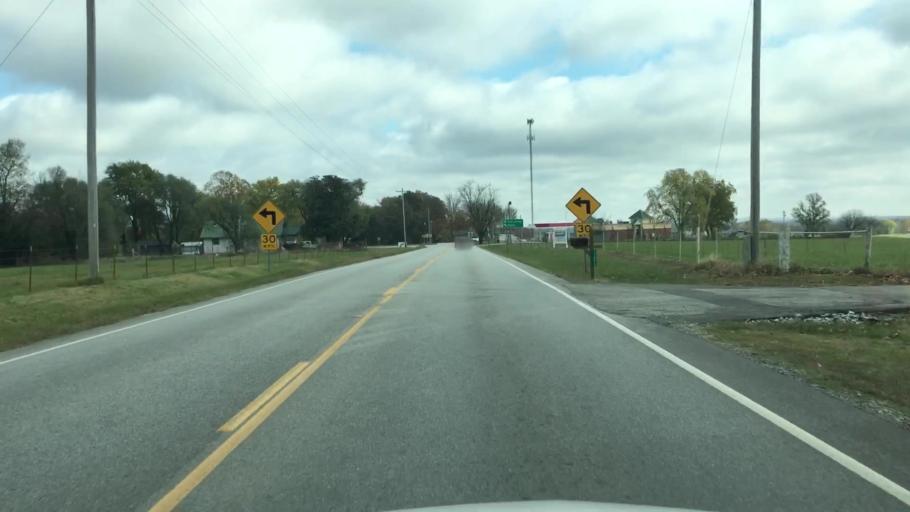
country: US
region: Arkansas
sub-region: Benton County
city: Centerton
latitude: 36.2616
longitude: -94.3538
